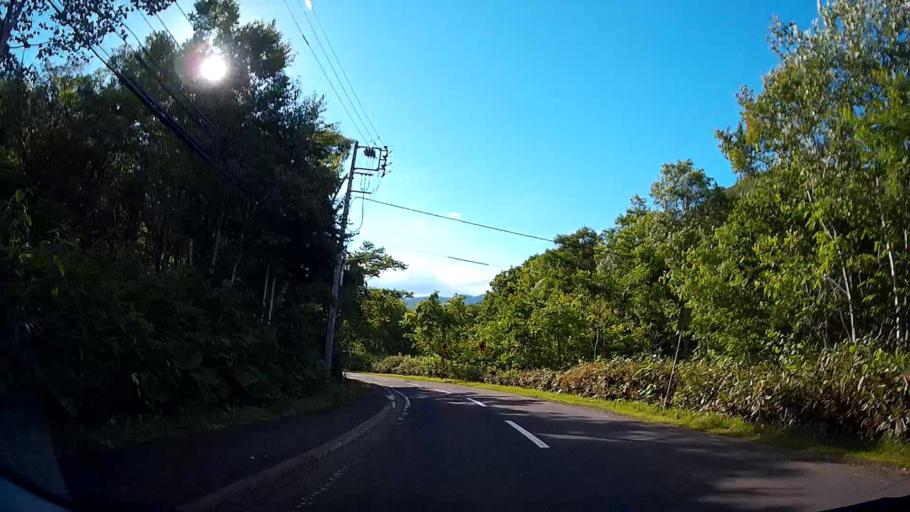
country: JP
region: Hokkaido
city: Sapporo
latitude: 42.9748
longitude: 141.1428
